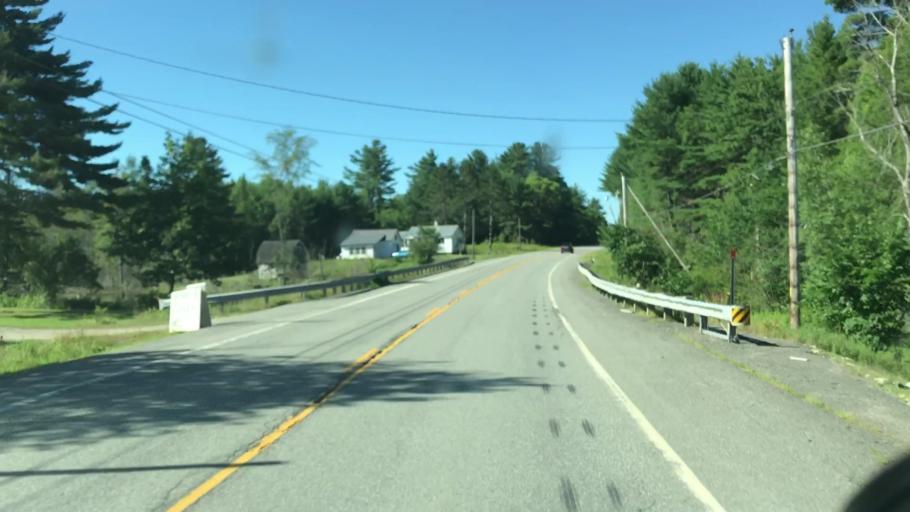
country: US
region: Maine
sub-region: Penobscot County
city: Howland
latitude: 45.2875
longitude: -68.6244
